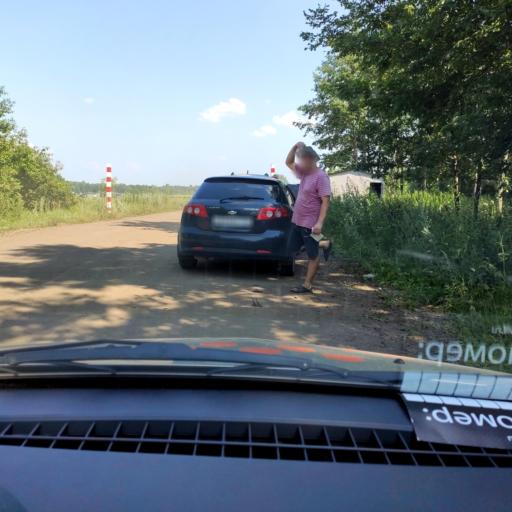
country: RU
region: Bashkortostan
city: Avdon
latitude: 54.6543
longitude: 55.8064
